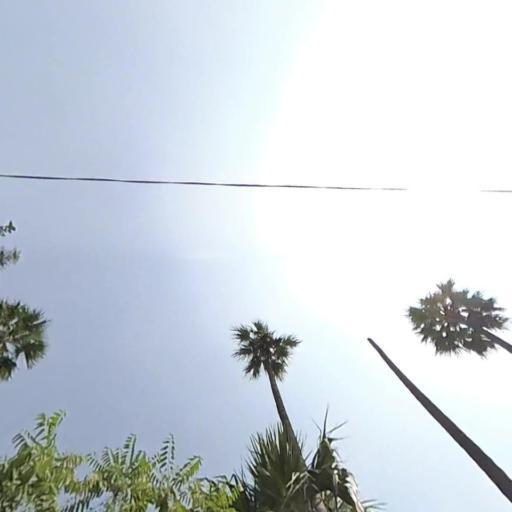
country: IN
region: Telangana
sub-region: Nalgonda
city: Nalgonda
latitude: 17.2116
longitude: 79.1574
